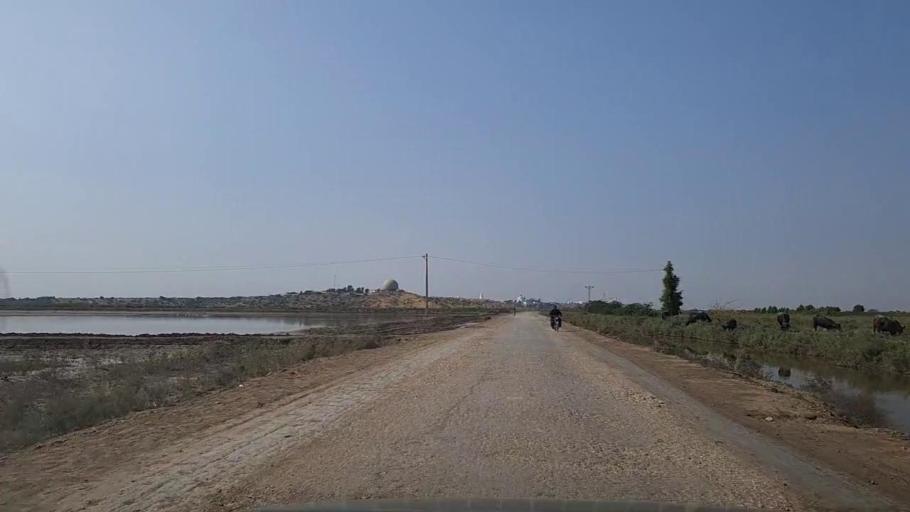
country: PK
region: Sindh
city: Chuhar Jamali
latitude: 24.5496
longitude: 67.8961
